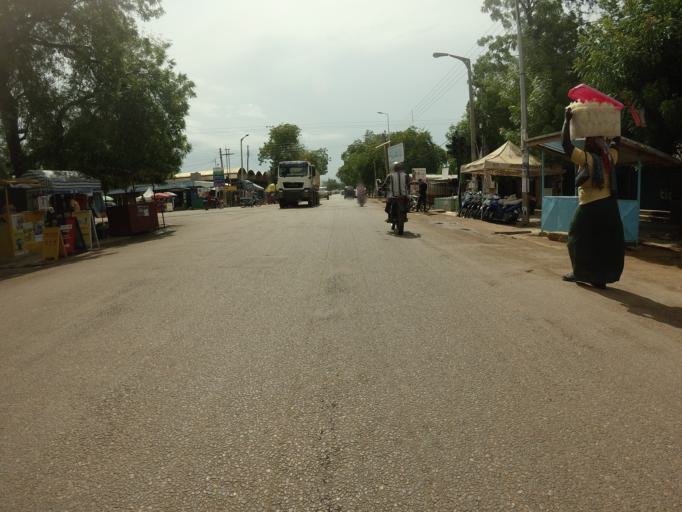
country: GH
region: Upper East
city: Bolgatanga
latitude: 10.7826
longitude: -0.8512
